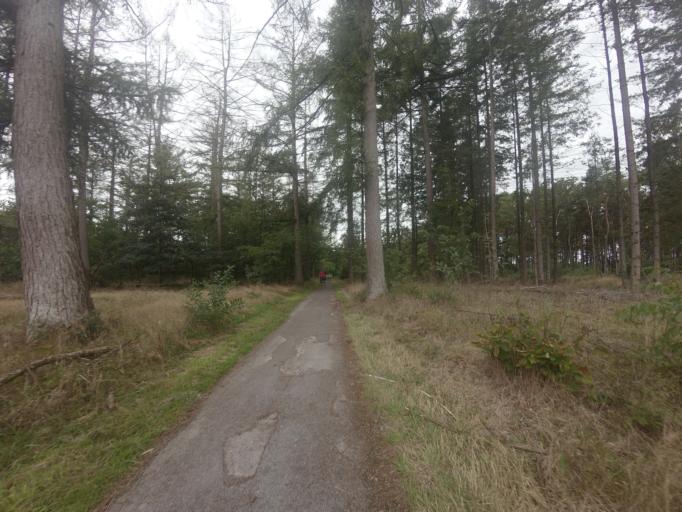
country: NL
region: Drenthe
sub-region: Gemeente Westerveld
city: Dwingeloo
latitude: 52.9083
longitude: 6.3117
